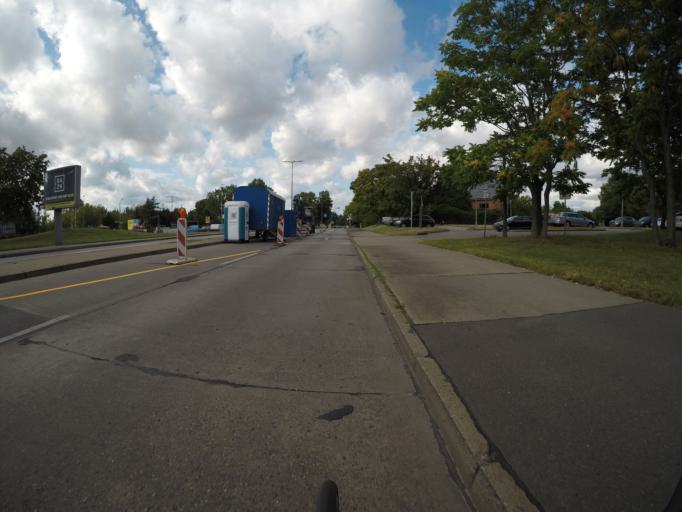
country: DE
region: Brandenburg
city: Ahrensfelde
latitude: 52.5726
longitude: 13.5676
